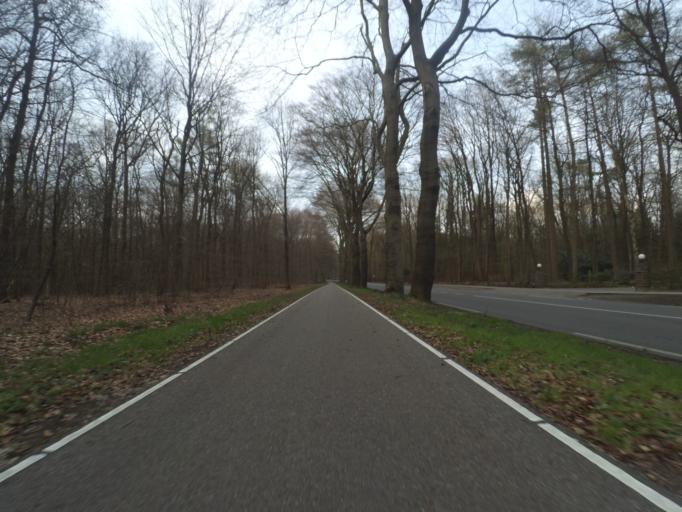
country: NL
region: Gelderland
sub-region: Gemeente Apeldoorn
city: Beekbergen
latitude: 52.1359
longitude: 5.8841
